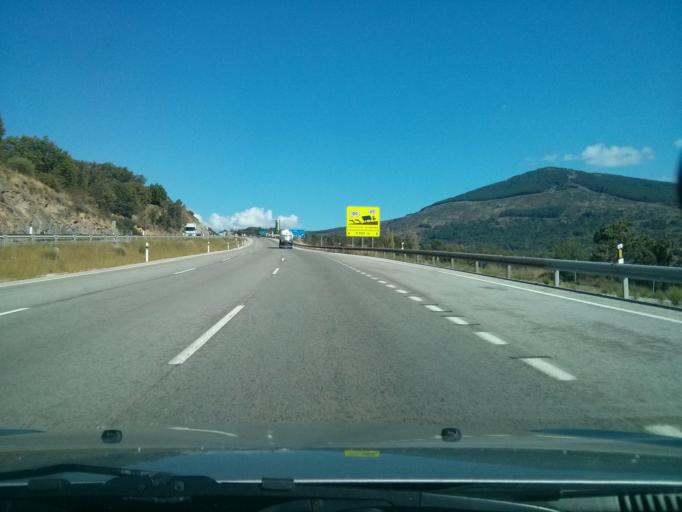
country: ES
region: Madrid
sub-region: Provincia de Madrid
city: Horcajo de la Sierra
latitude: 41.0845
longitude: -3.5965
